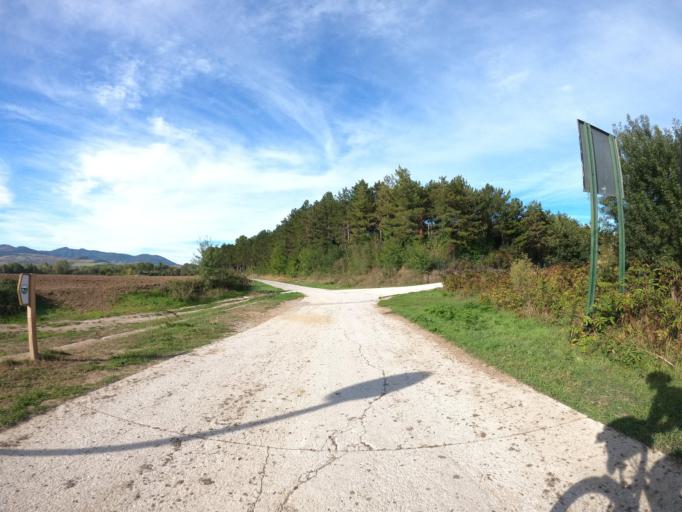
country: ES
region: Navarre
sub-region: Provincia de Navarra
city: Oltza
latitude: 42.8030
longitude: -1.7692
